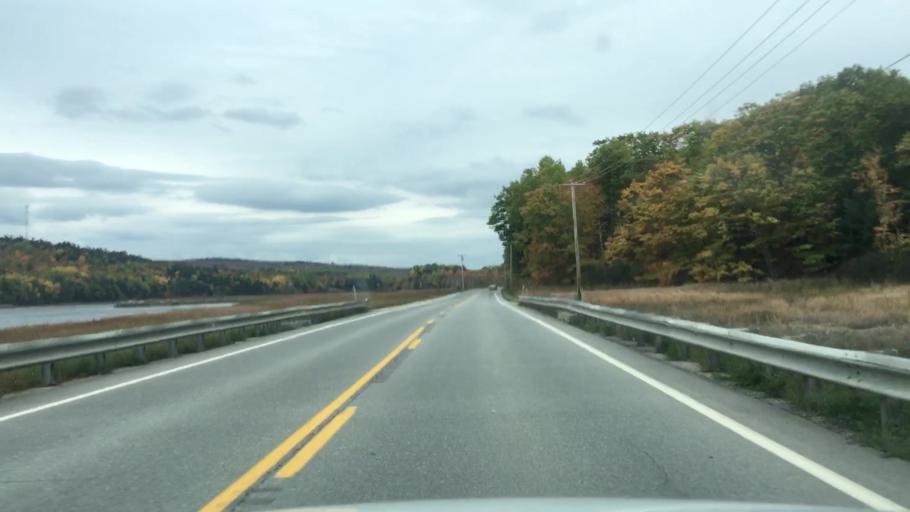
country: US
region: Maine
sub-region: Waldo County
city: Frankfort
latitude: 44.5878
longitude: -68.8647
